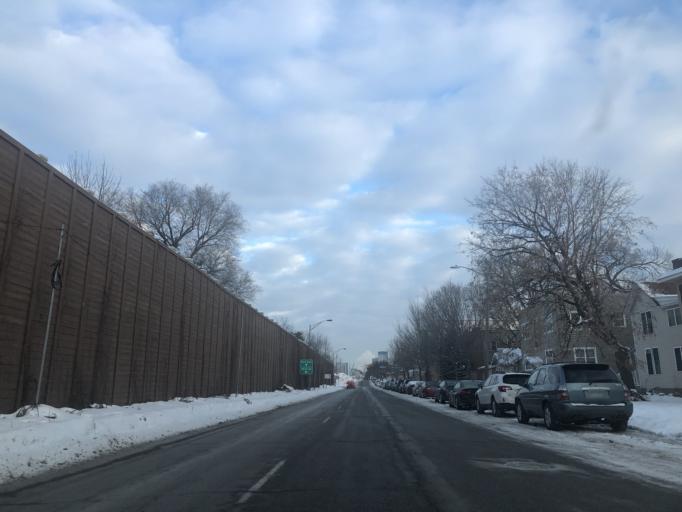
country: US
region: Minnesota
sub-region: Hennepin County
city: Minneapolis
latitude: 44.9380
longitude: -93.2741
